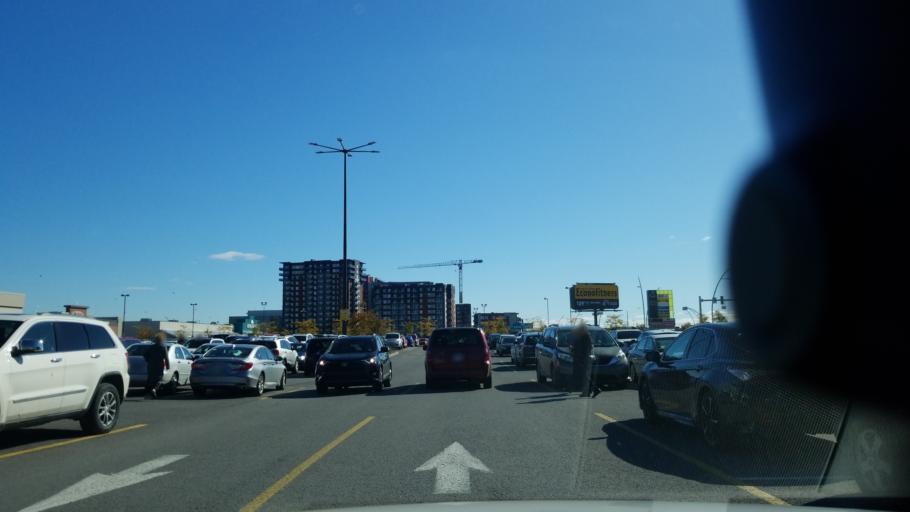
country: CA
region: Quebec
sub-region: Laval
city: Laval
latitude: 45.5633
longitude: -73.7293
